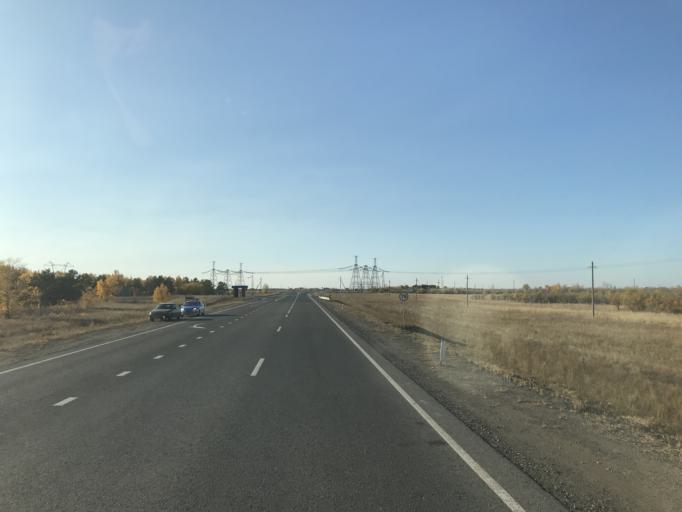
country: KZ
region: Pavlodar
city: Koktobe
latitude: 51.9071
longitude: 77.3654
